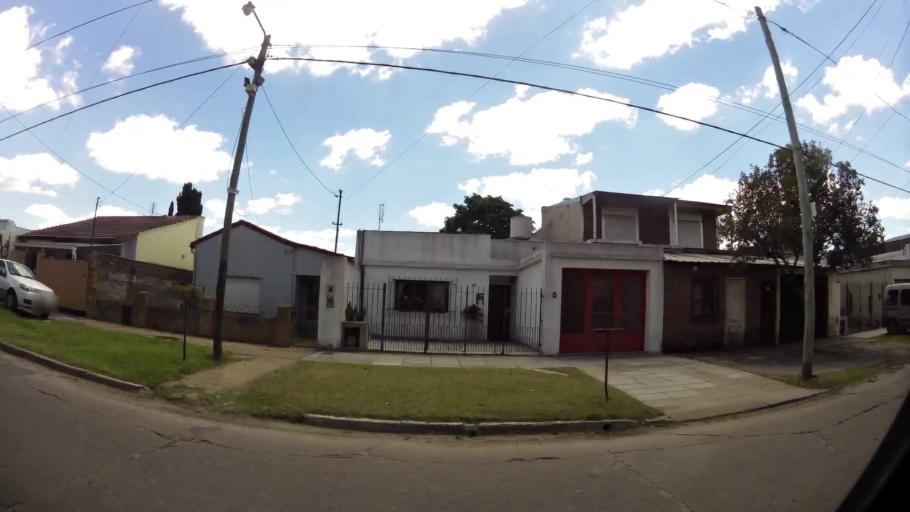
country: AR
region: Buenos Aires
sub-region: Partido de Lomas de Zamora
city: Lomas de Zamora
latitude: -34.7334
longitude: -58.4151
